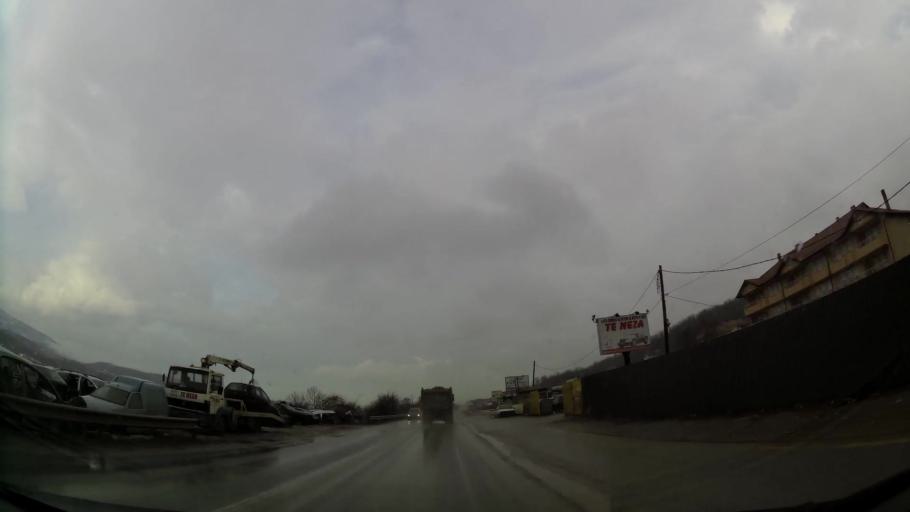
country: XK
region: Ferizaj
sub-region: Komuna e Kacanikut
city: Kacanik
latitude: 42.2410
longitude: 21.2435
